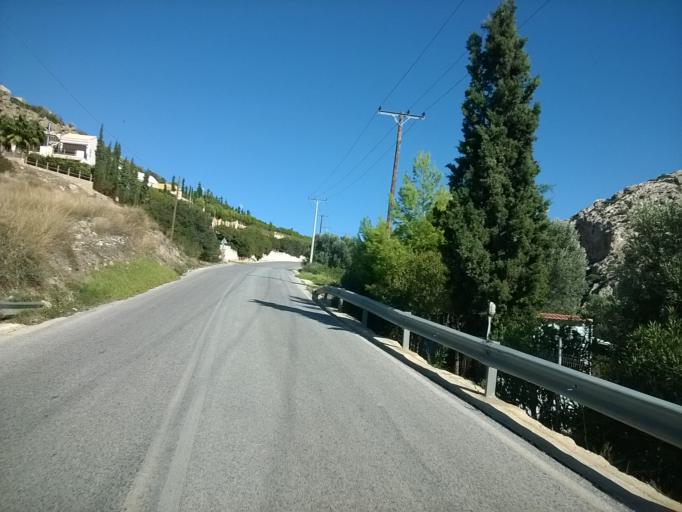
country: GR
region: Attica
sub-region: Nomarchia Anatolikis Attikis
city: Keratea
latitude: 37.7691
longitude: 23.9857
